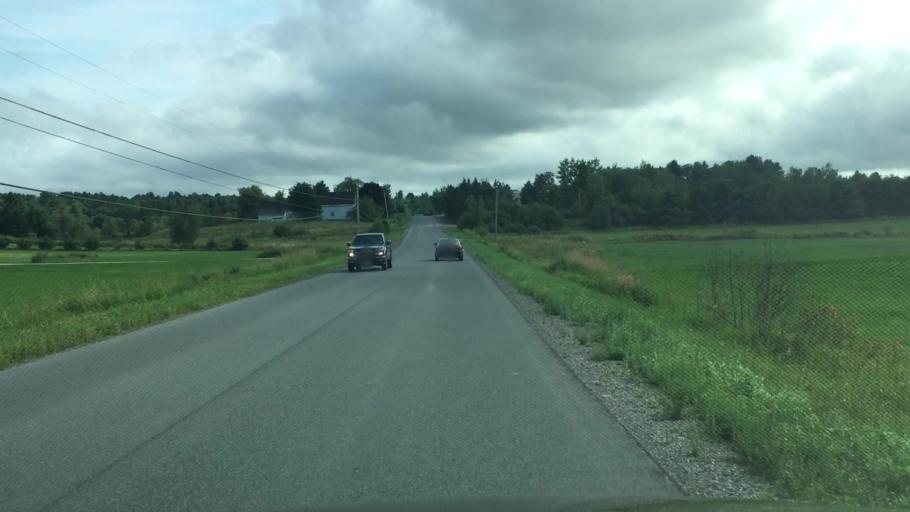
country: US
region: Maine
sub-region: Waldo County
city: Winterport
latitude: 44.6733
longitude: -68.8683
